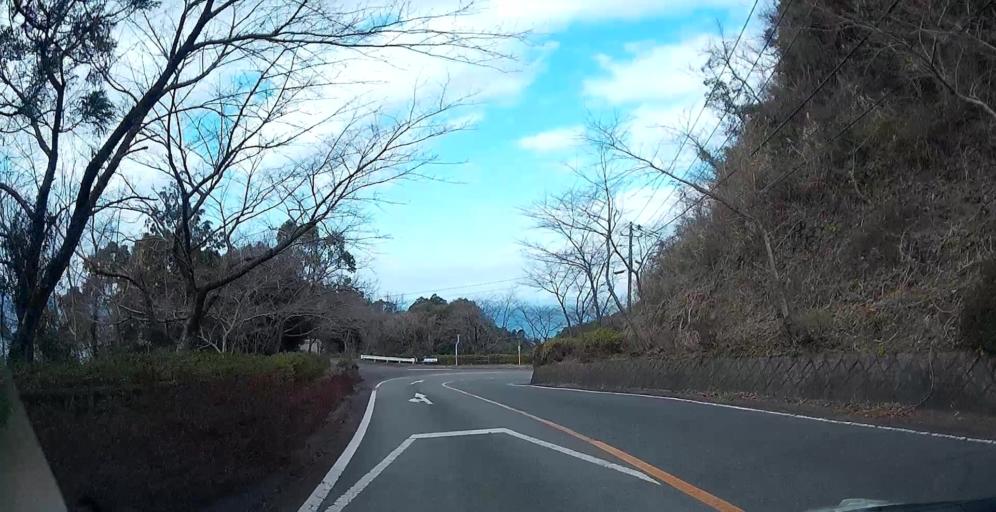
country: JP
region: Kumamoto
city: Yatsushiro
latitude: 32.3721
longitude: 130.5025
